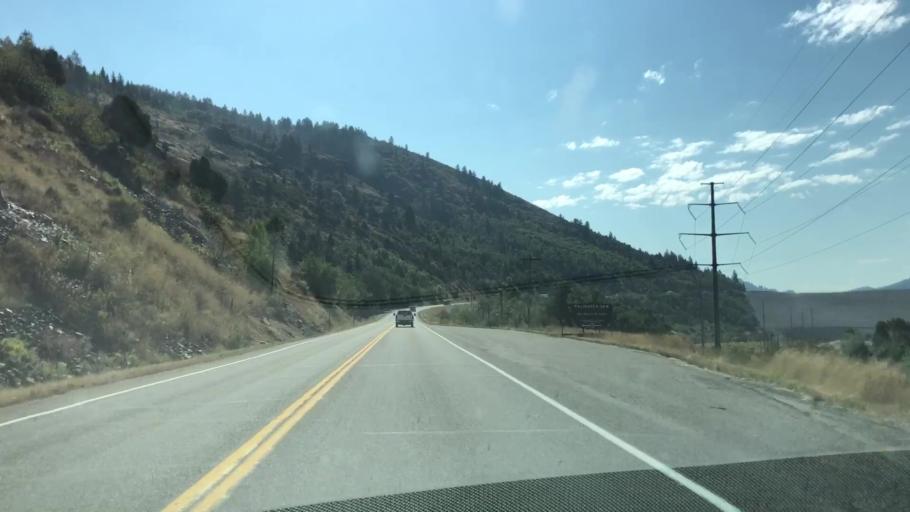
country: US
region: Idaho
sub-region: Teton County
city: Victor
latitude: 43.3449
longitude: -111.2067
